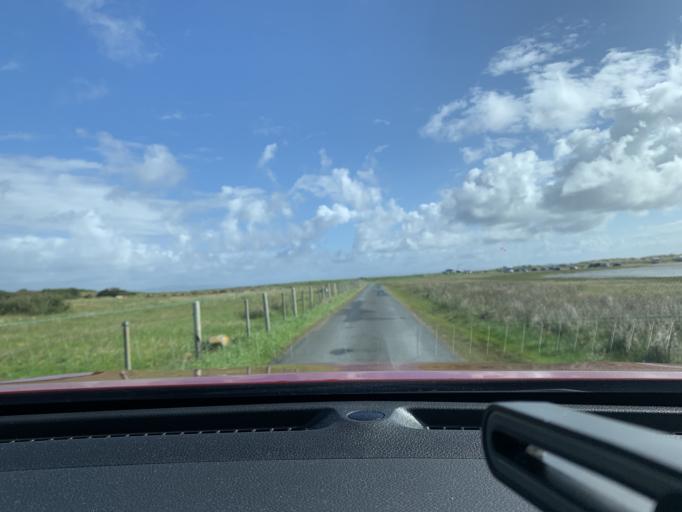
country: IE
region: Connaught
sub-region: Sligo
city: Strandhill
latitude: 54.4028
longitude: -8.5629
